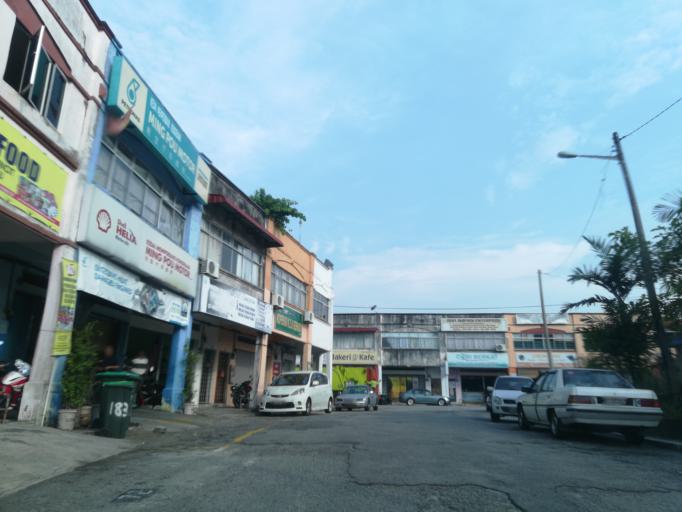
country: MY
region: Kedah
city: Kulim
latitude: 5.3902
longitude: 100.5647
